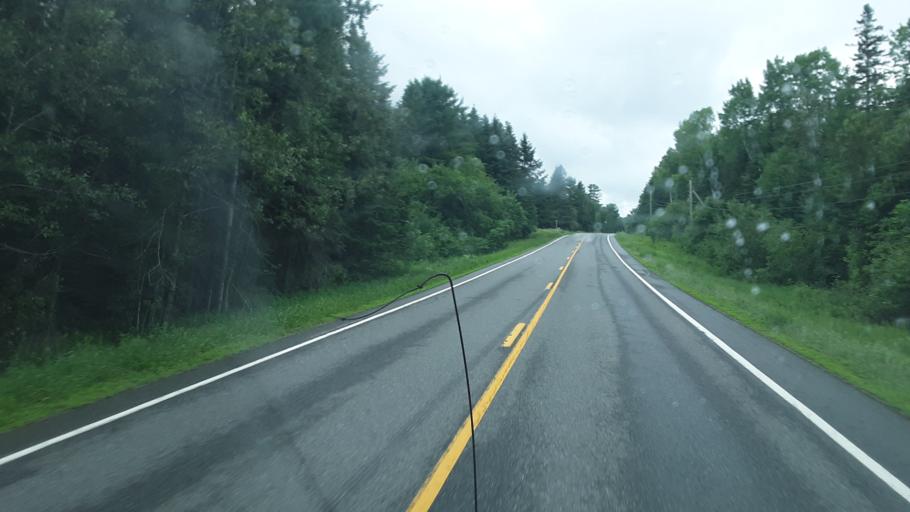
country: US
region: Maine
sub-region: Aroostook County
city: Presque Isle
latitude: 46.4738
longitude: -68.3884
